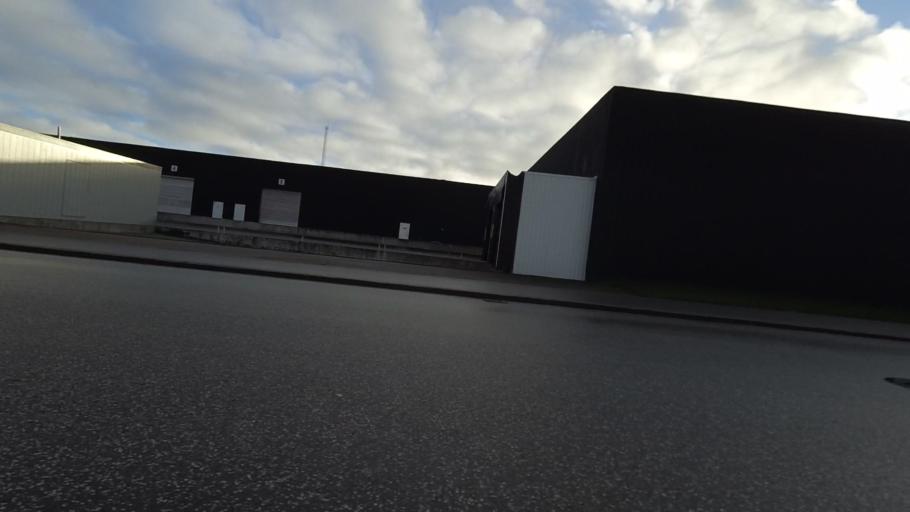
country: DK
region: Central Jutland
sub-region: Arhus Kommune
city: Tranbjerg
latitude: 56.1084
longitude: 10.1588
